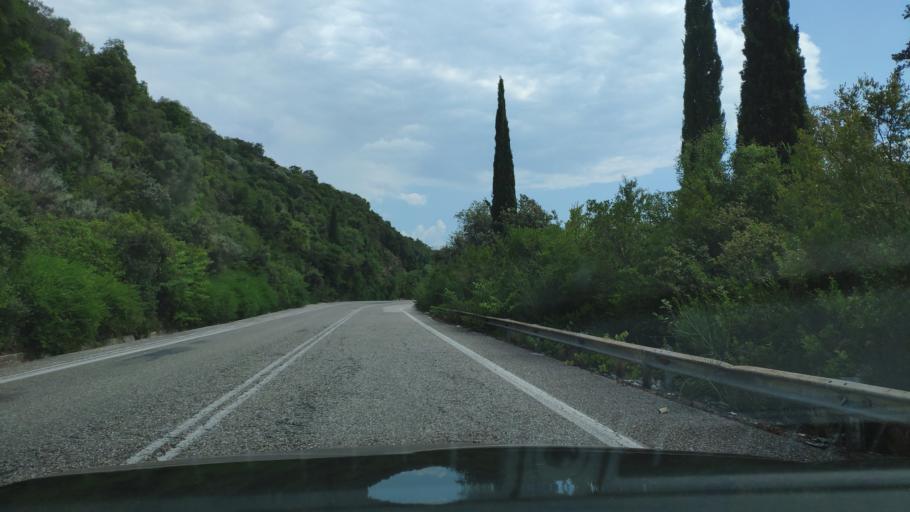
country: GR
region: West Greece
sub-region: Nomos Aitolias kai Akarnanias
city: Menidi
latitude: 39.0053
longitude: 21.1473
